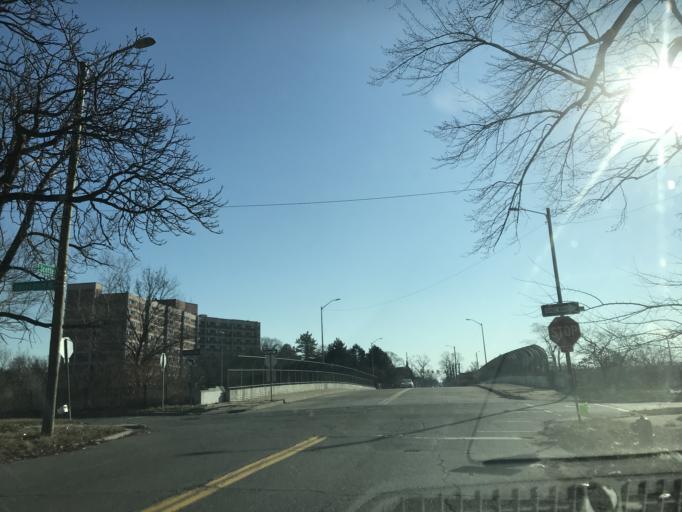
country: US
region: Michigan
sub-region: Wayne County
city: Highland Park
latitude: 42.3464
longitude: -83.1122
